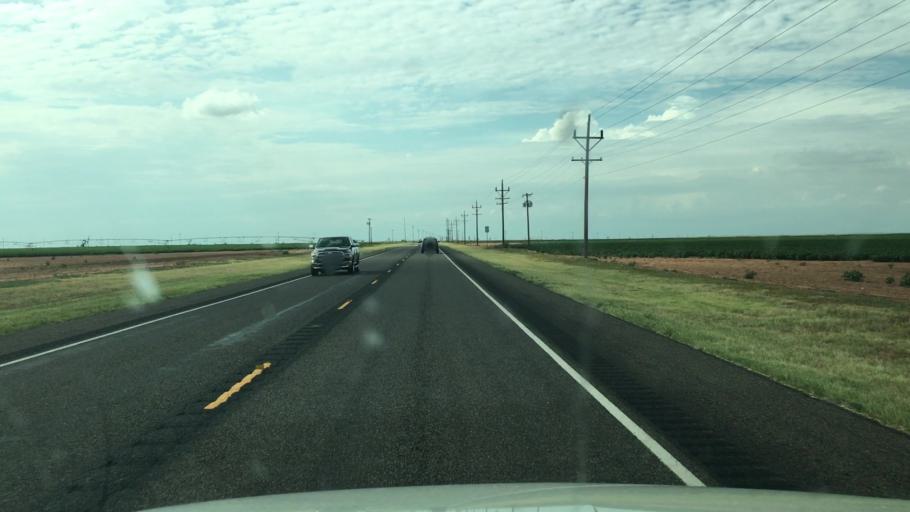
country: US
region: Texas
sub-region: Dawson County
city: Lamesa
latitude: 32.8852
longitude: -102.0848
